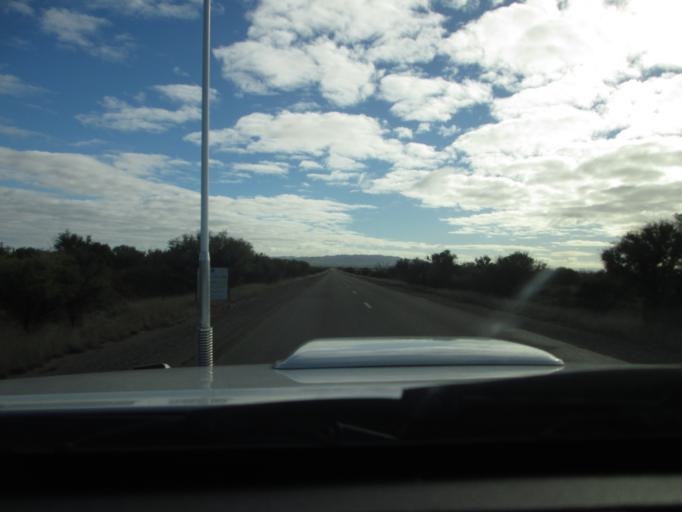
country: AU
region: South Australia
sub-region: Peterborough
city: Peterborough
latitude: -32.7112
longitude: 138.6104
